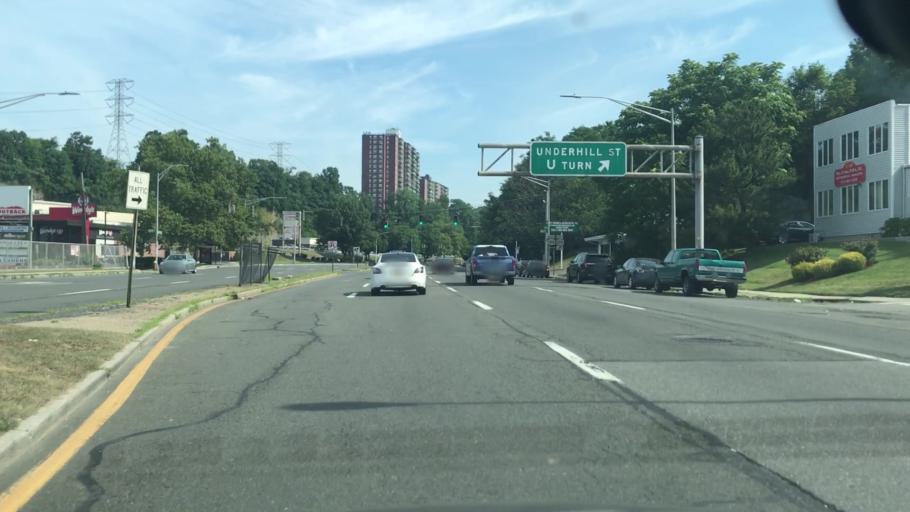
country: US
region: New York
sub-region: Westchester County
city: Tuckahoe
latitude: 40.9578
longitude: -73.8417
